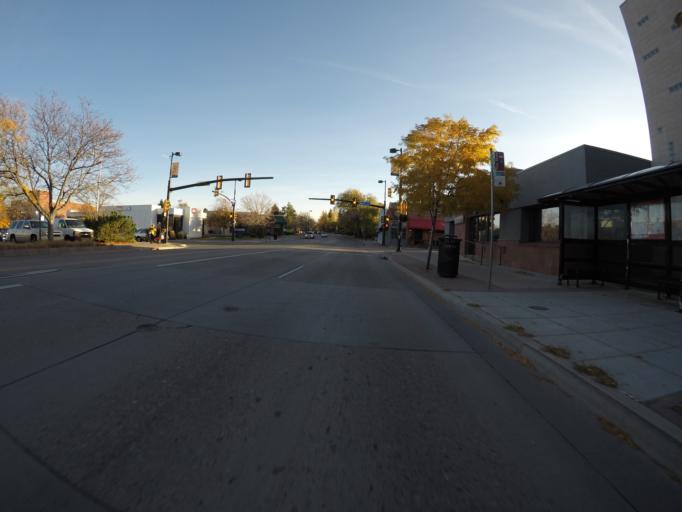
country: US
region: Colorado
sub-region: Boulder County
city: Boulder
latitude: 40.0248
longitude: -105.2822
